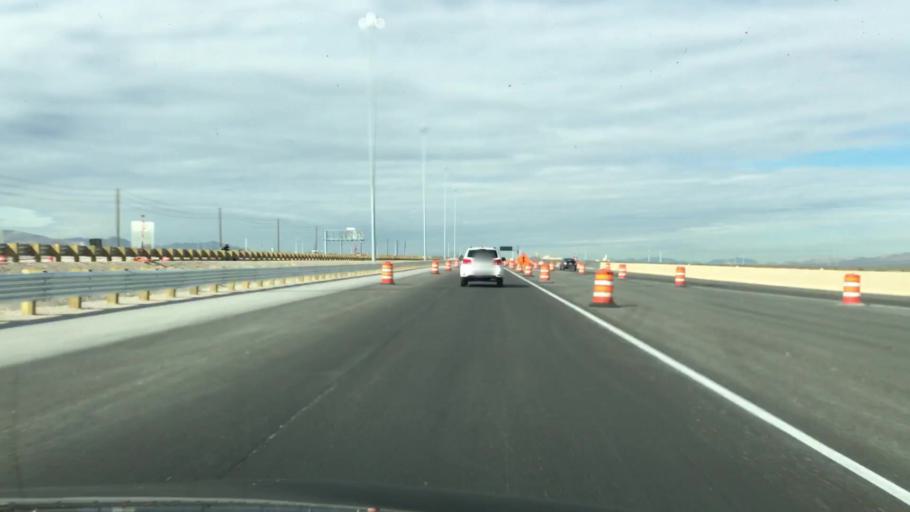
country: US
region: Nevada
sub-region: Clark County
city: Summerlin South
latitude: 36.3177
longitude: -115.3034
